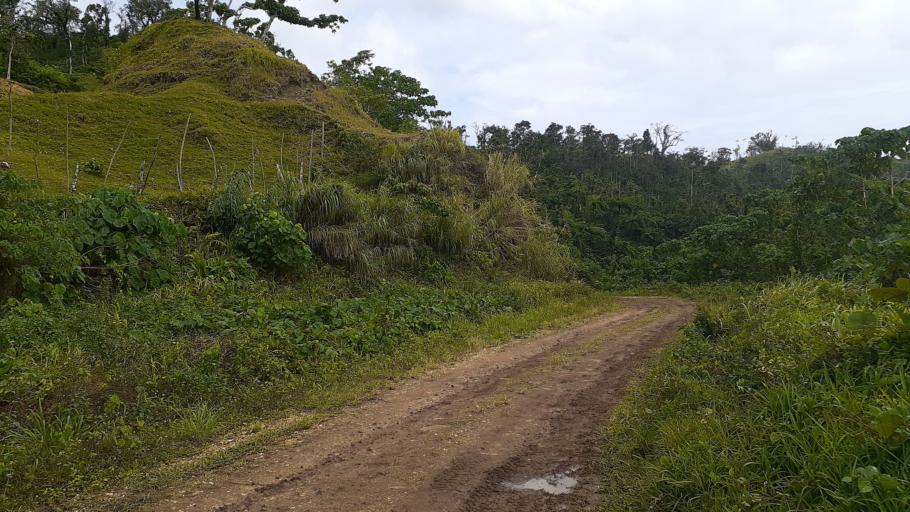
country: VU
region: Penama
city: Saratamata
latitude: -15.9658
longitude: 168.2159
